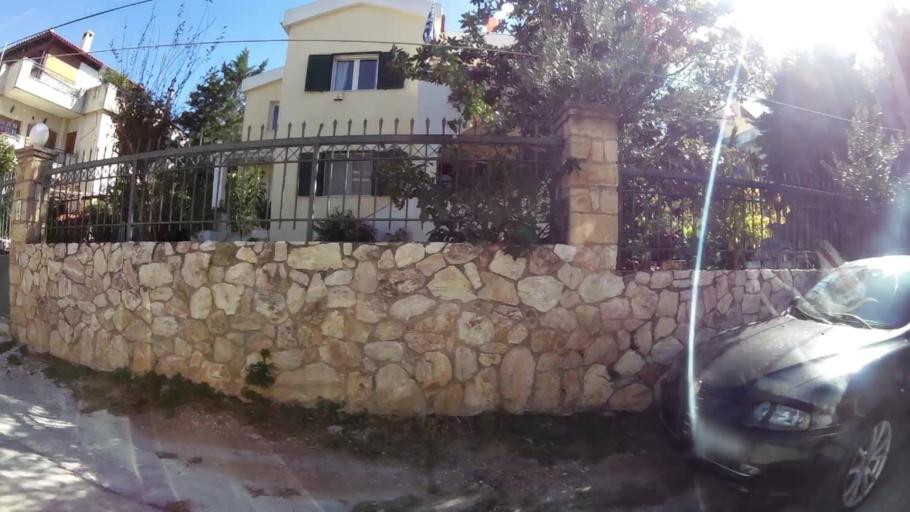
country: GR
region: Attica
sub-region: Nomarchia Athinas
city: Kifisia
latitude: 38.0858
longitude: 23.7956
